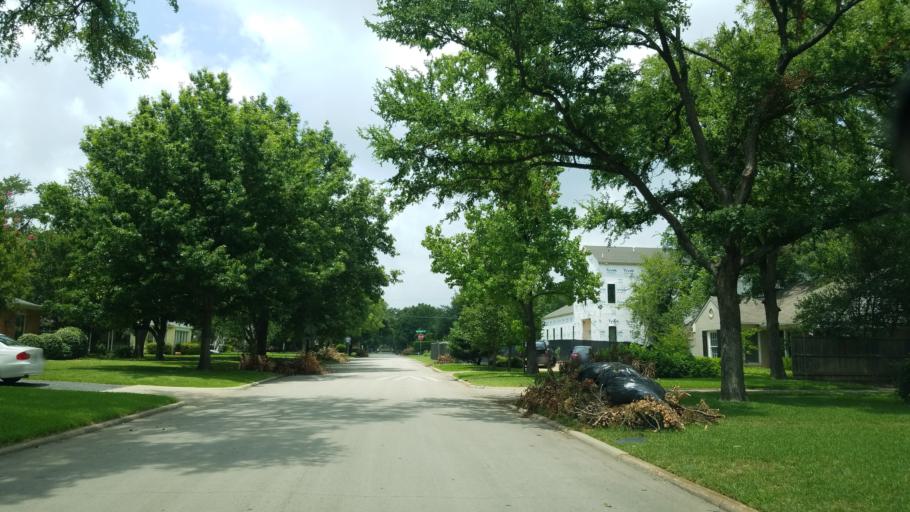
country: US
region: Texas
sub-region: Dallas County
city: University Park
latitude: 32.8405
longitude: -96.8231
